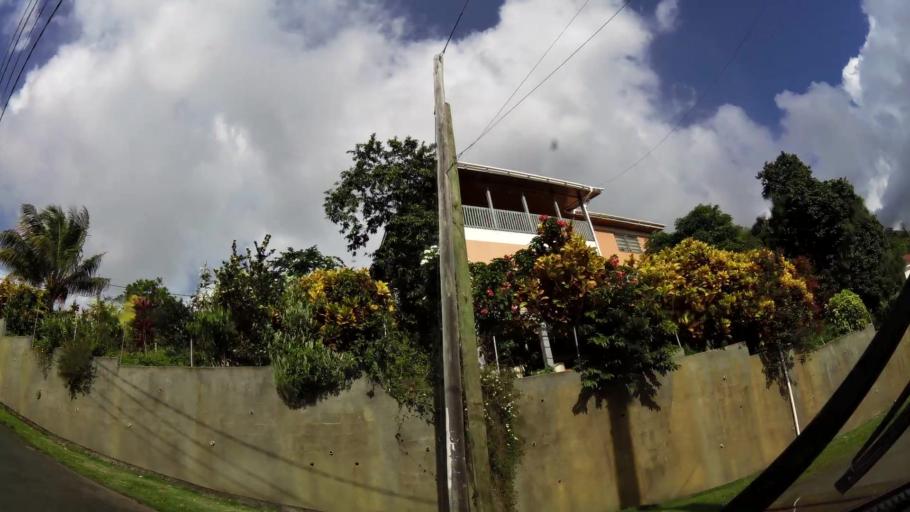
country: DM
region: Saint George
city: Roseau
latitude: 15.3074
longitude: -61.3722
